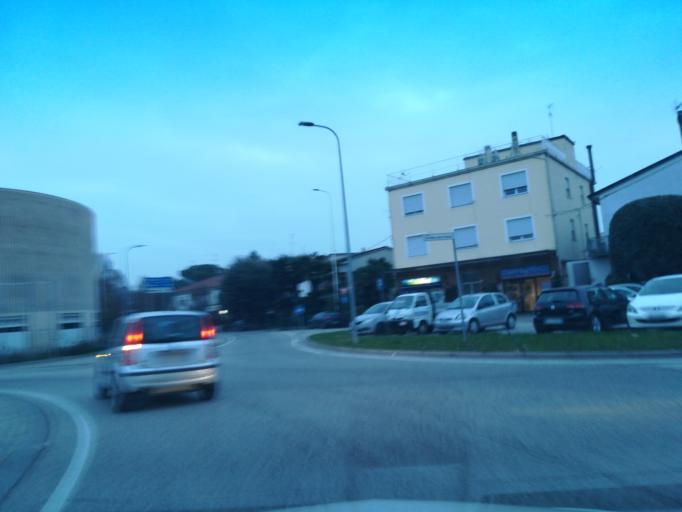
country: IT
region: Emilia-Romagna
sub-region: Provincia di Ravenna
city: Faenza
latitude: 44.2955
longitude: 11.8881
